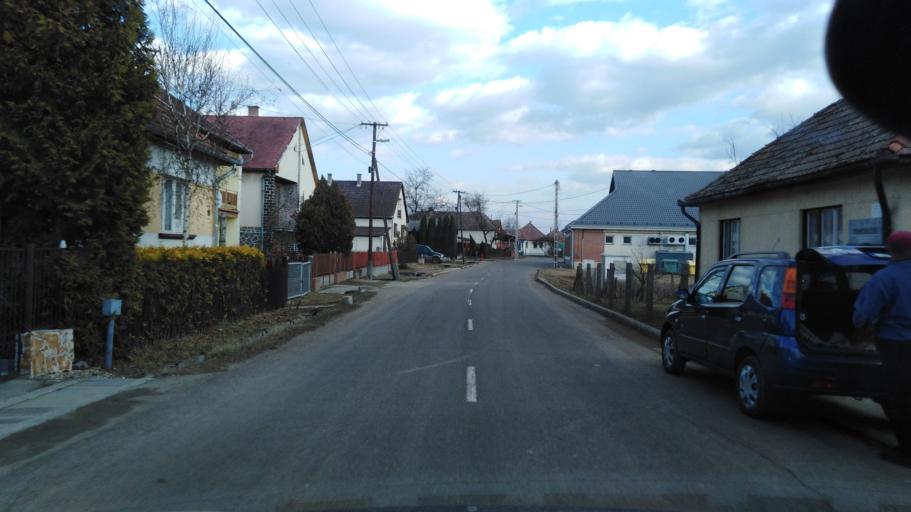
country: HU
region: Nograd
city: Matranovak
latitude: 48.1472
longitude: 19.9656
